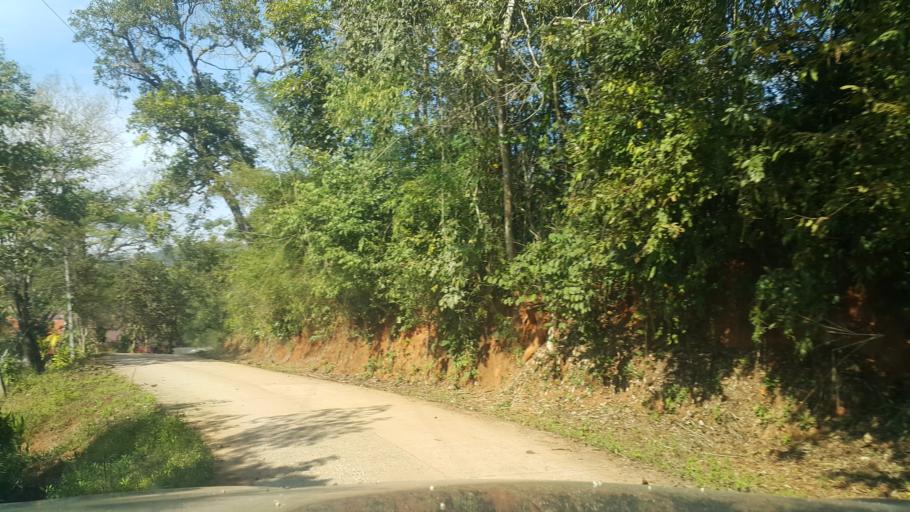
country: TH
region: Chiang Mai
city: Samoeng
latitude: 18.9488
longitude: 98.6748
